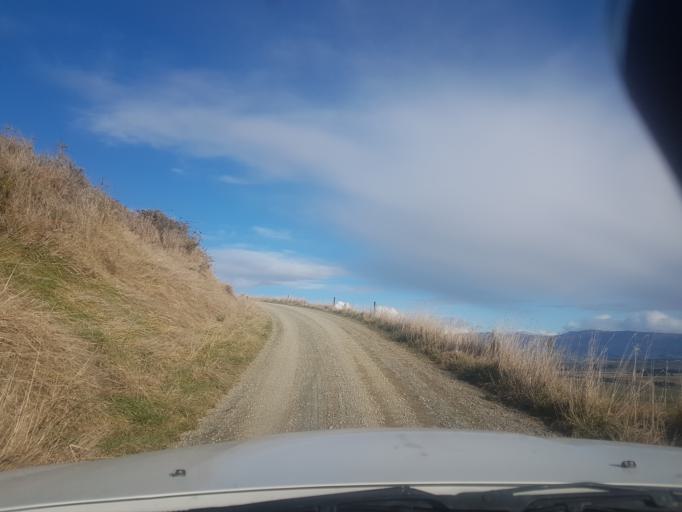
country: NZ
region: Canterbury
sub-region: Timaru District
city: Pleasant Point
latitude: -44.1670
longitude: 170.8810
